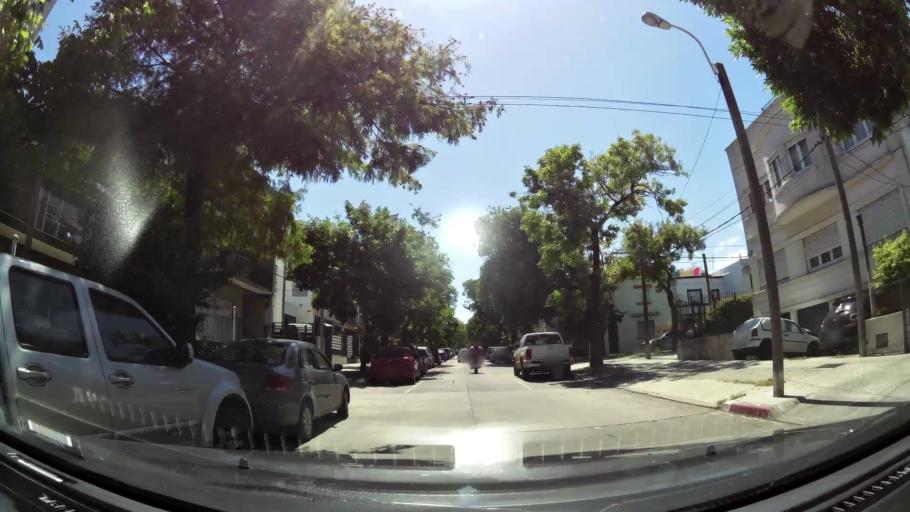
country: UY
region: Montevideo
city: Montevideo
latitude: -34.9231
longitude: -56.1565
